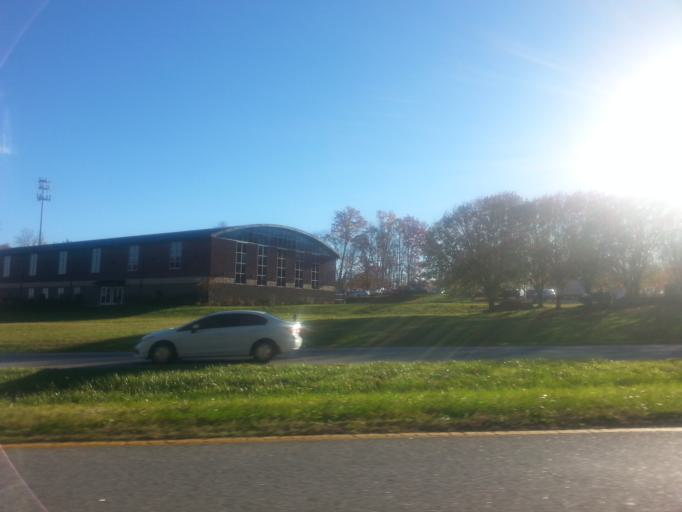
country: US
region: Tennessee
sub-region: Blount County
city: Eagleton Village
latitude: 35.8638
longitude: -83.9596
